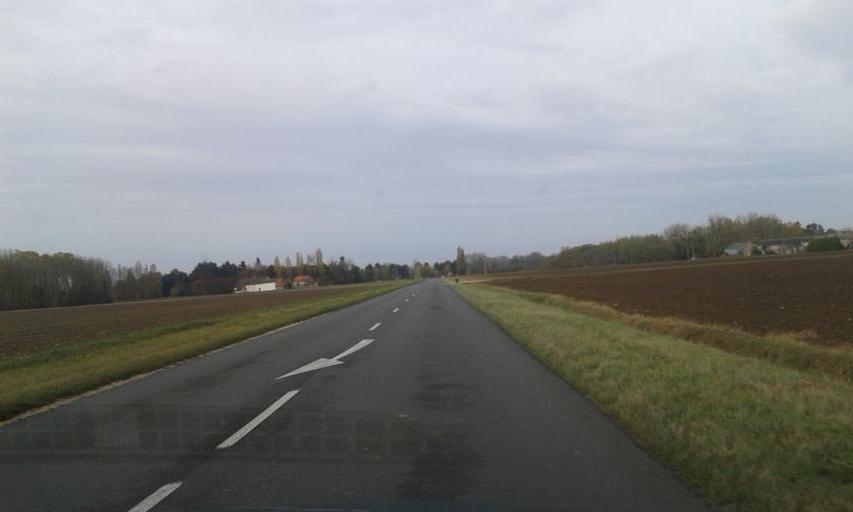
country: FR
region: Centre
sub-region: Departement du Loiret
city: Lailly-en-Val
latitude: 47.7758
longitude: 1.6677
